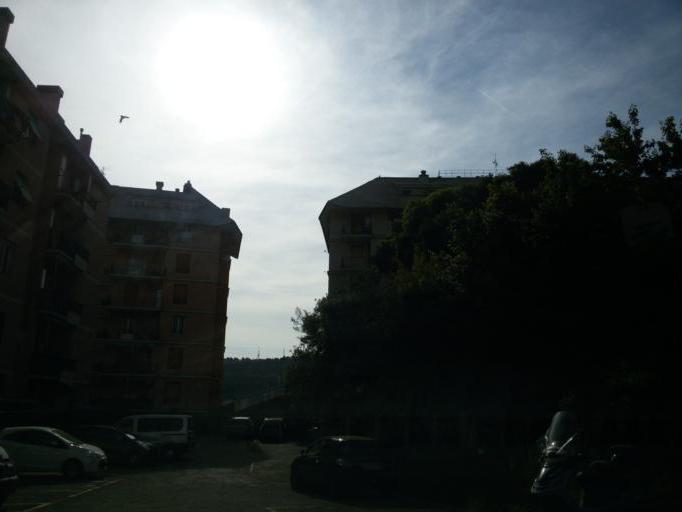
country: IT
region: Liguria
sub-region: Provincia di Genova
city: Genoa
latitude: 44.4193
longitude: 8.9599
